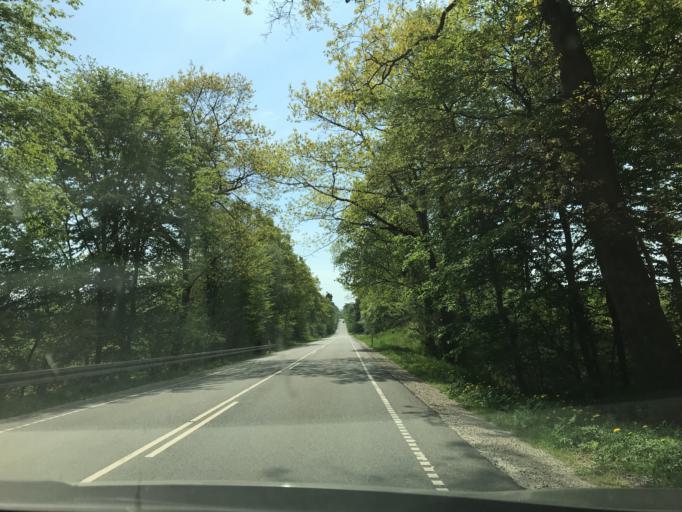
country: DK
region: South Denmark
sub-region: Middelfart Kommune
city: Ejby
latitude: 55.3994
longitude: 9.9023
